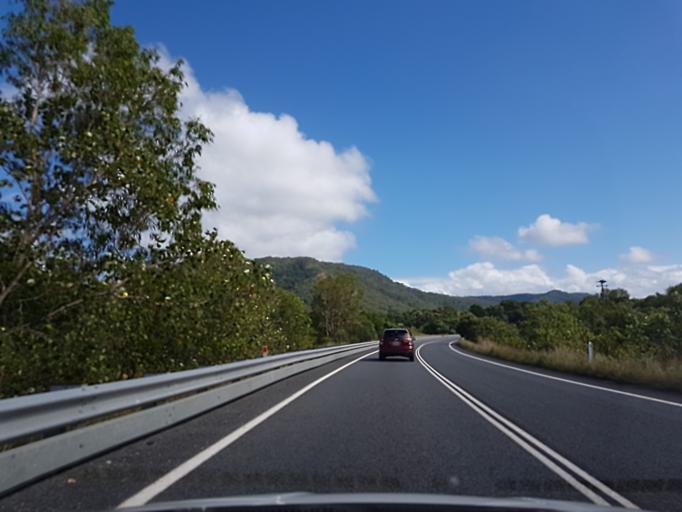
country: AU
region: Queensland
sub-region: Cairns
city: Port Douglas
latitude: -16.5530
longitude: 145.4779
